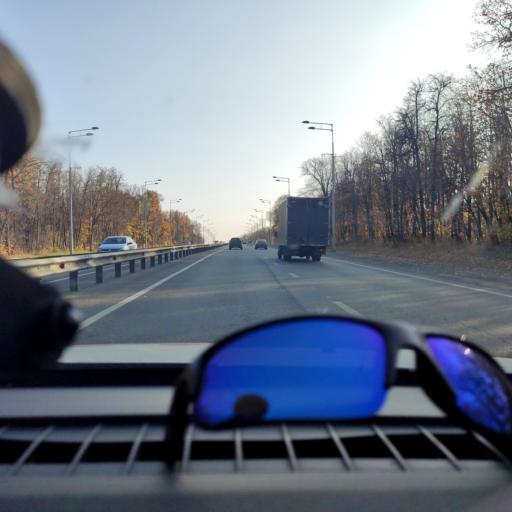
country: RU
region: Samara
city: Novosemeykino
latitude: 53.3221
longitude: 50.2305
